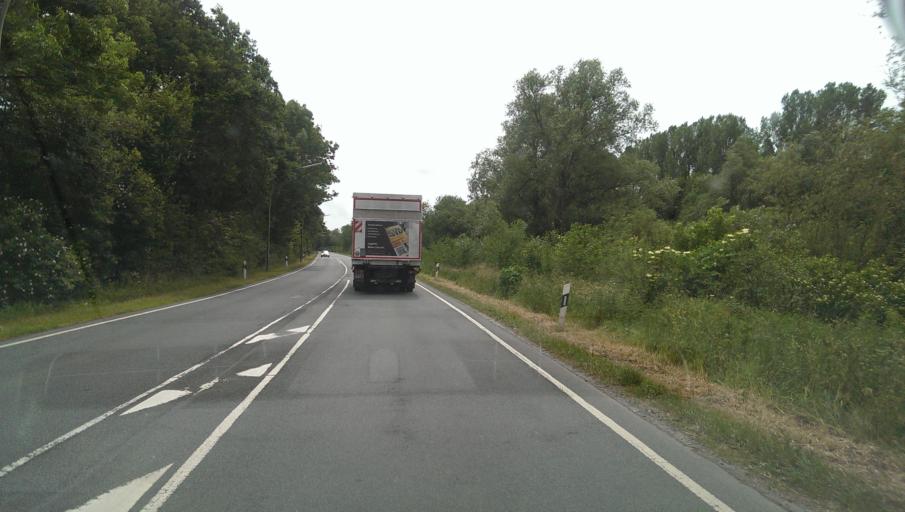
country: DE
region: Lower Saxony
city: Langen
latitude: 53.5832
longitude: 8.5707
